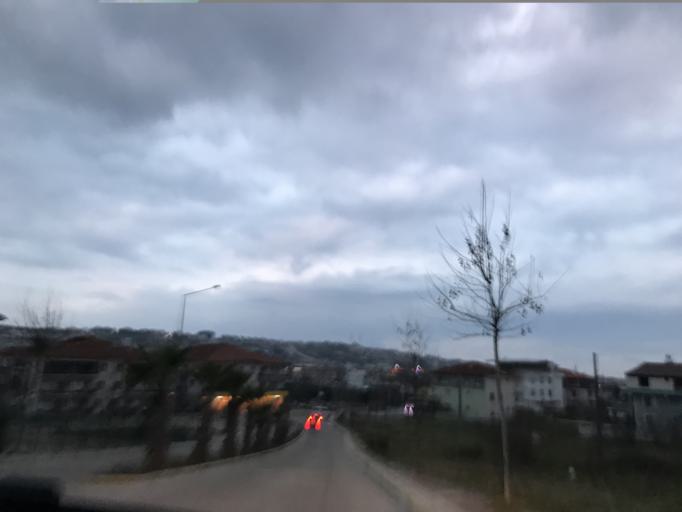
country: TR
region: Yalova
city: Yalova
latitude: 40.6376
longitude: 29.2624
